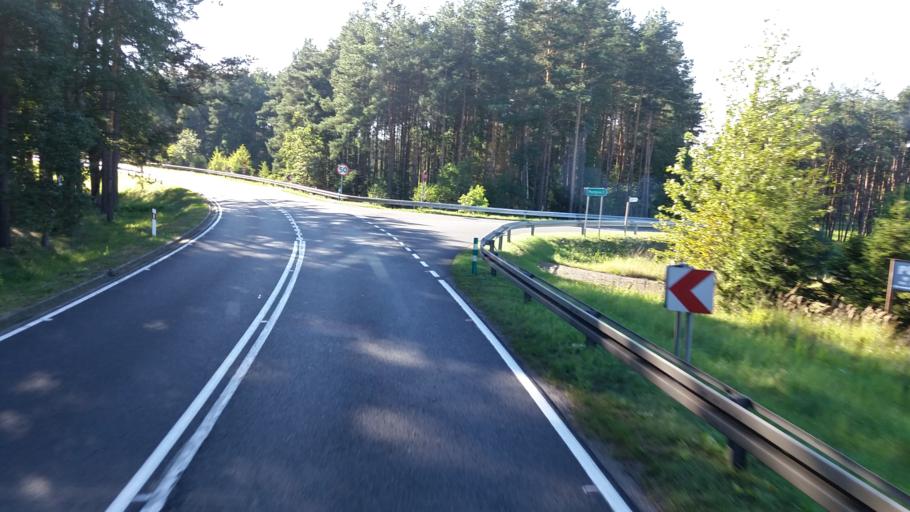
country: PL
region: West Pomeranian Voivodeship
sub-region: Powiat choszczenski
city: Drawno
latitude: 53.3046
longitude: 15.7858
